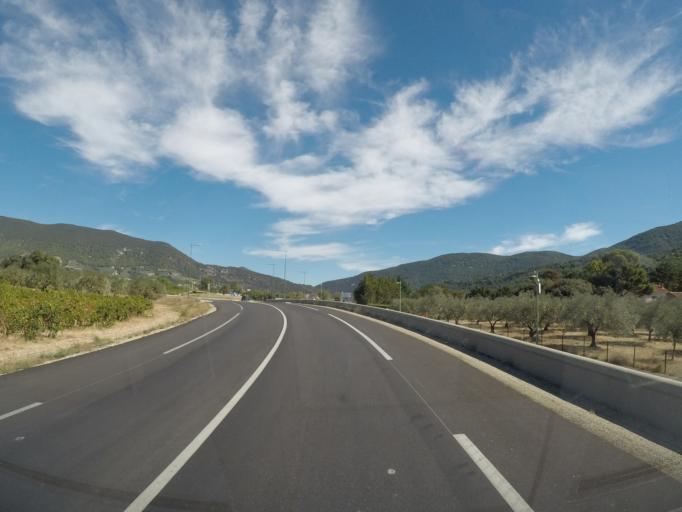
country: FR
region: Rhone-Alpes
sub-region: Departement de la Drome
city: Nyons
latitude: 44.3491
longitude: 5.1153
